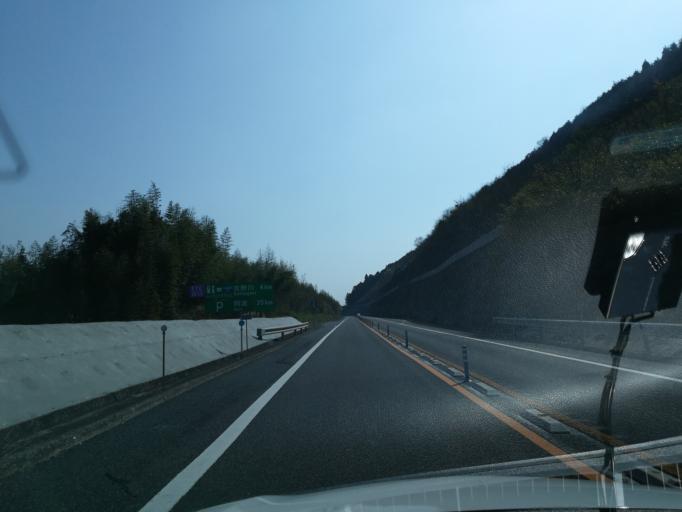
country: JP
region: Tokushima
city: Ikedacho
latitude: 34.0315
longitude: 133.8554
